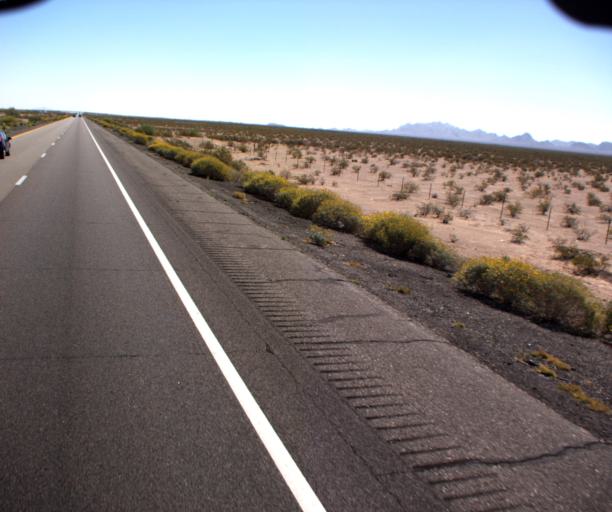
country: US
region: Arizona
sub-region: La Paz County
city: Salome
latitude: 33.5996
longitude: -113.5585
